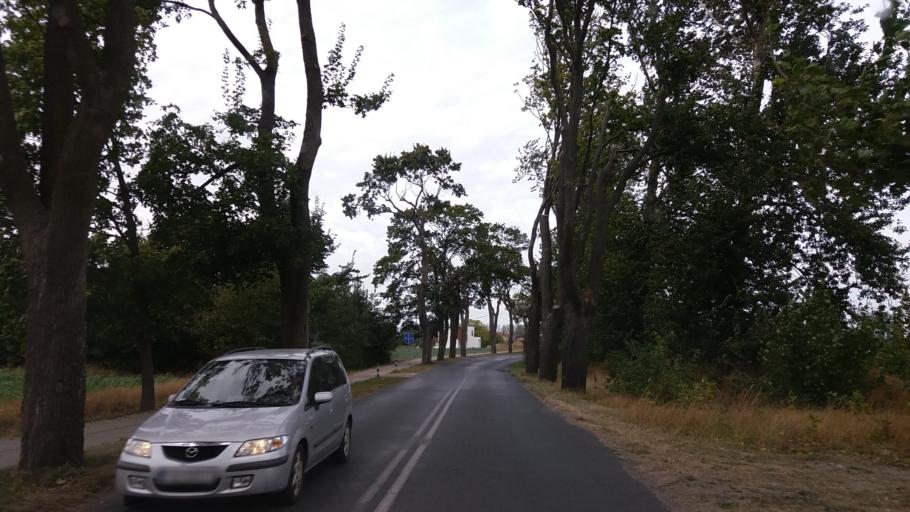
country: PL
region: Lubusz
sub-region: Powiat strzelecko-drezdenecki
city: Strzelce Krajenskie
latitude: 52.8974
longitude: 15.5071
